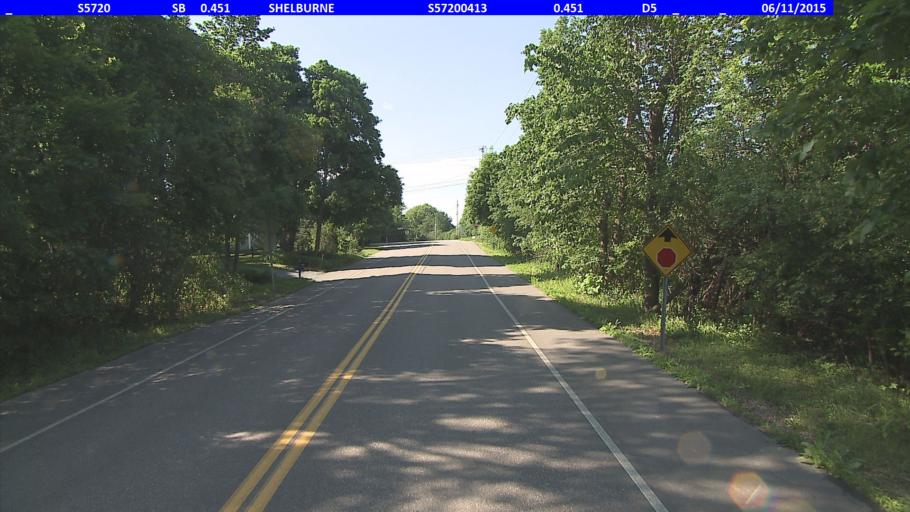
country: US
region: Vermont
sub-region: Chittenden County
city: South Burlington
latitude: 44.3745
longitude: -73.2024
